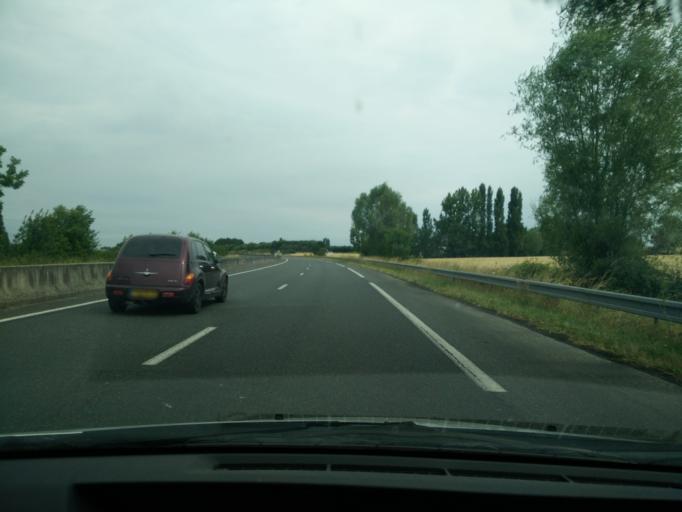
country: FR
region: Pays de la Loire
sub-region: Departement de Maine-et-Loire
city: Saint-Jean
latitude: 47.2425
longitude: -0.3211
